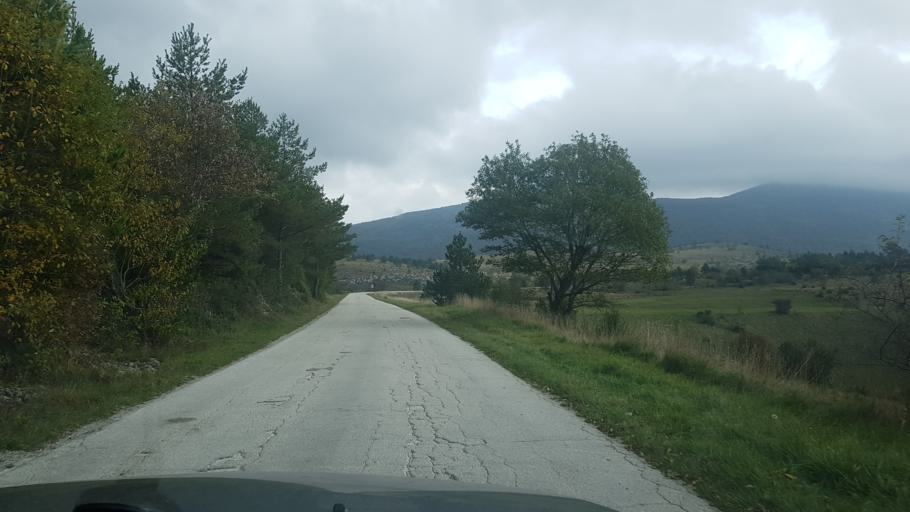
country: HR
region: Istarska
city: Buzet
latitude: 45.4988
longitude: 14.0060
